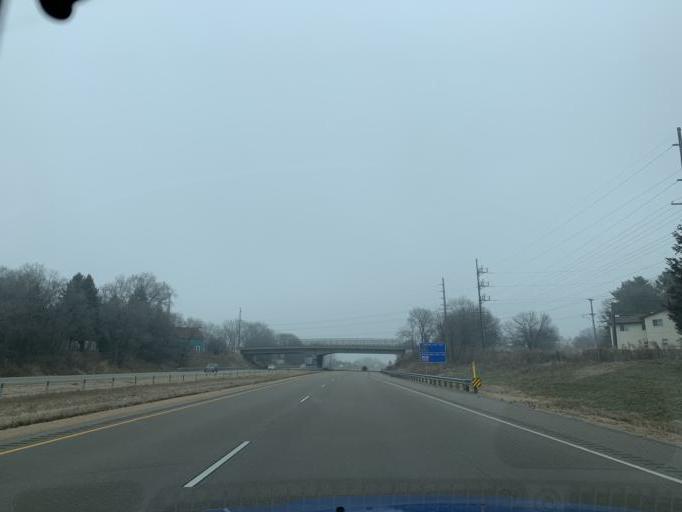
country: US
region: Wisconsin
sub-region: Dane County
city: Sun Prairie
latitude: 43.1909
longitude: -89.2277
